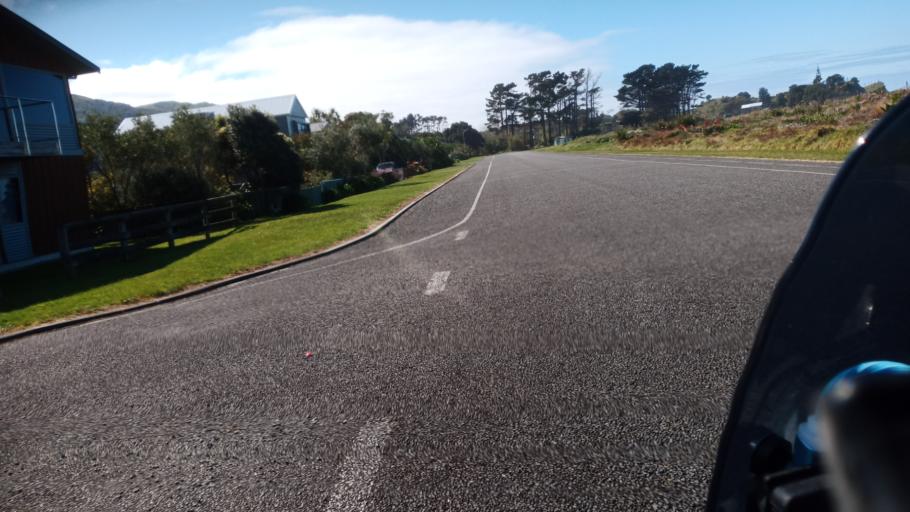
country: NZ
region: Gisborne
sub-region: Gisborne District
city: Gisborne
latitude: -39.0164
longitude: 177.8852
